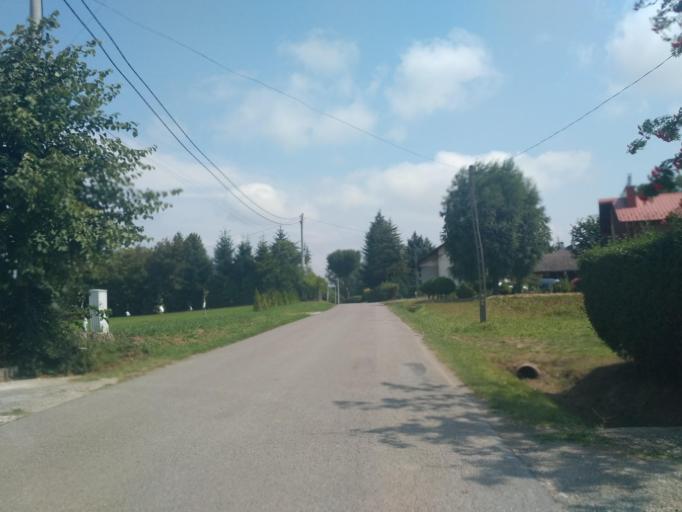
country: PL
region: Subcarpathian Voivodeship
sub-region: Powiat lancucki
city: Kraczkowa
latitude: 50.0373
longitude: 22.1817
